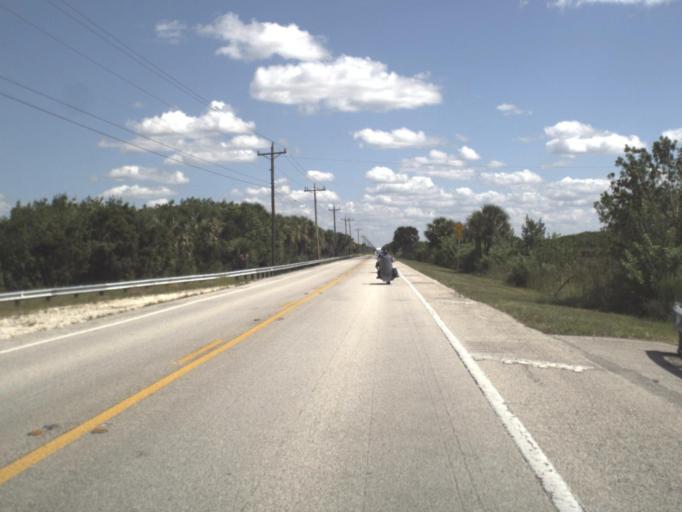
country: US
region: Florida
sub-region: Collier County
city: Marco
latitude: 25.9376
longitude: -81.4601
